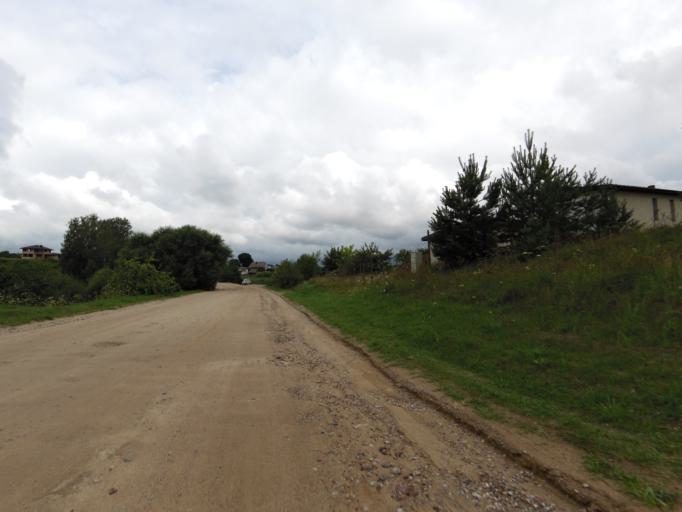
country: LT
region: Vilnius County
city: Pilaite
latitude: 54.7002
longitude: 25.1611
